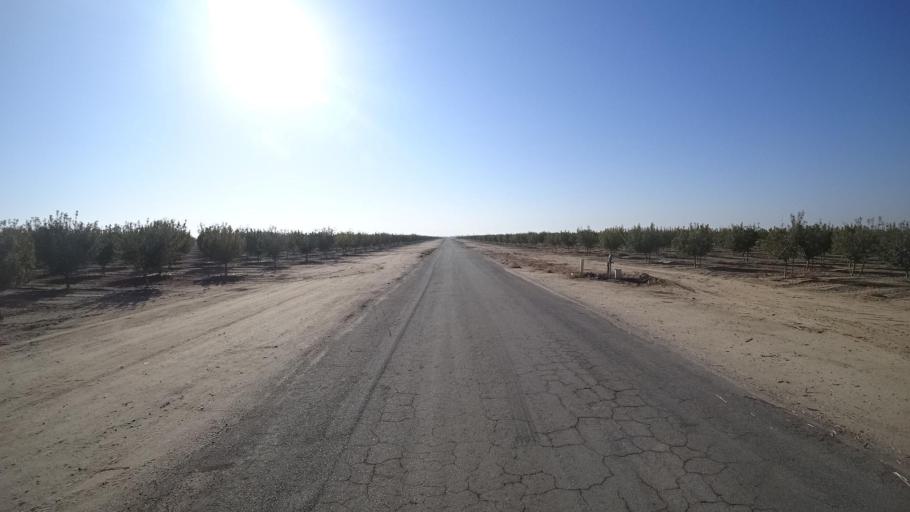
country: US
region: California
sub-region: Kern County
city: Delano
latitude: 35.7540
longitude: -119.2319
